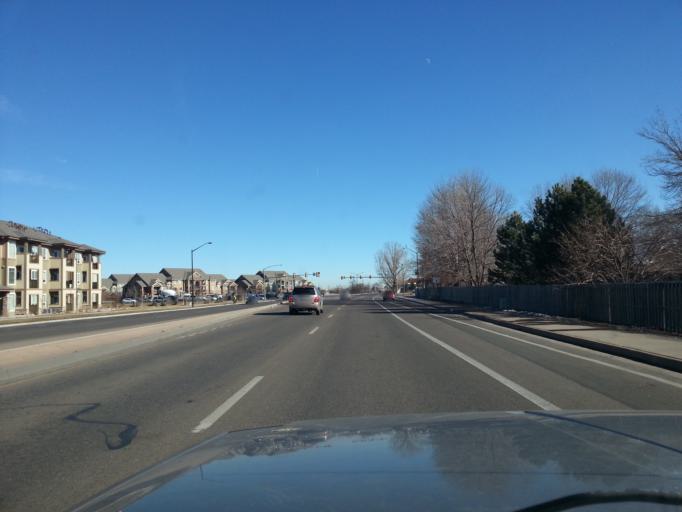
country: US
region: Colorado
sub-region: Larimer County
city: Fort Collins
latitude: 40.5526
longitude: -105.0412
